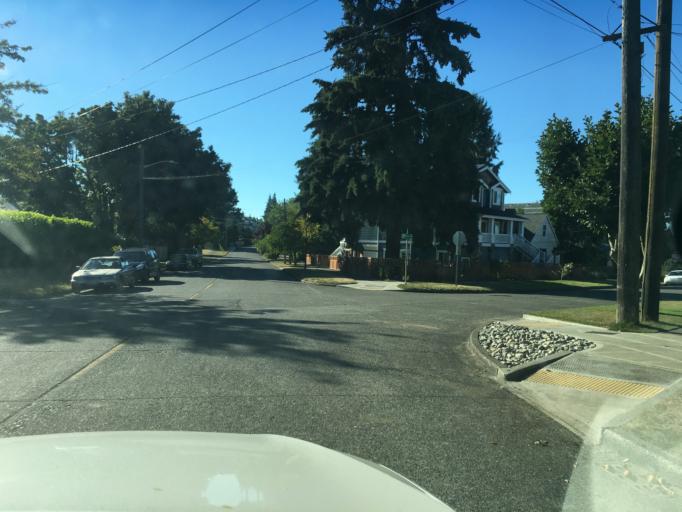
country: US
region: Washington
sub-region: King County
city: Shoreline
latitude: 47.6875
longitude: -122.3942
